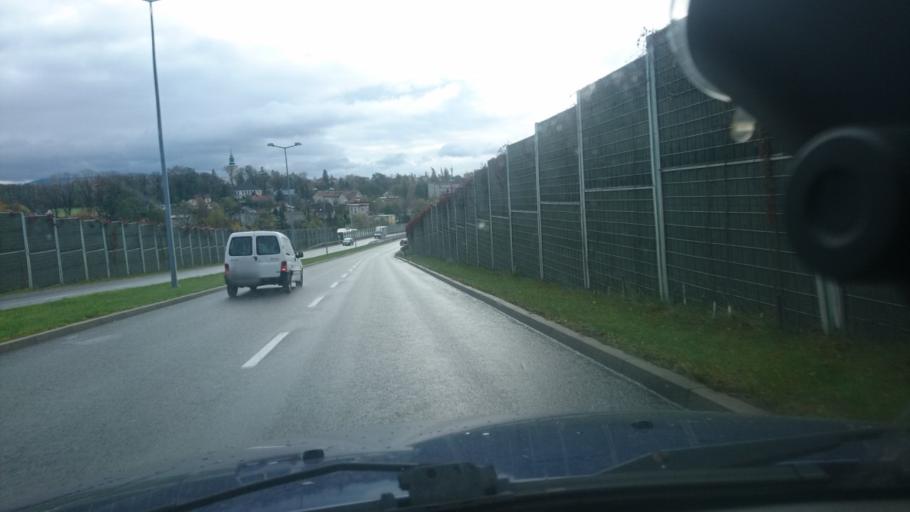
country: PL
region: Silesian Voivodeship
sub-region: Bielsko-Biala
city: Bielsko-Biala
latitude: 49.8269
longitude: 19.0144
